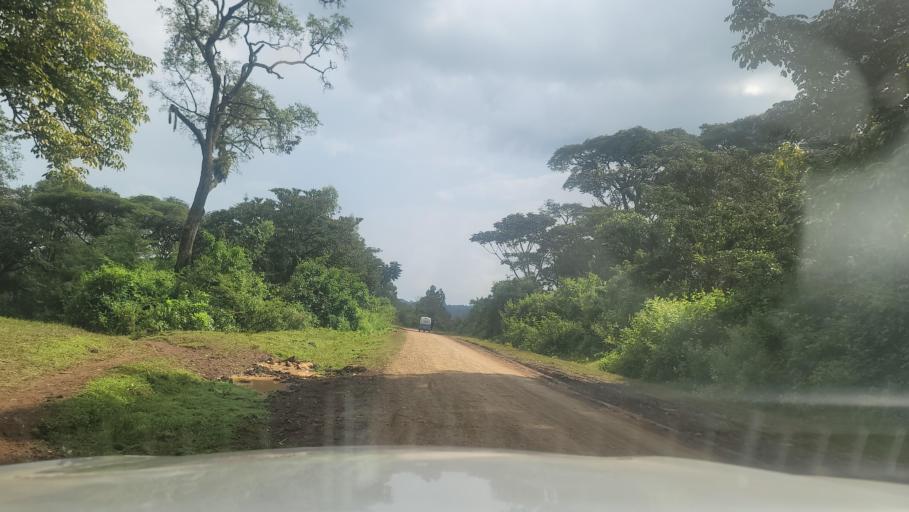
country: ET
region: Oromiya
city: Agaro
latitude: 7.7139
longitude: 36.2570
